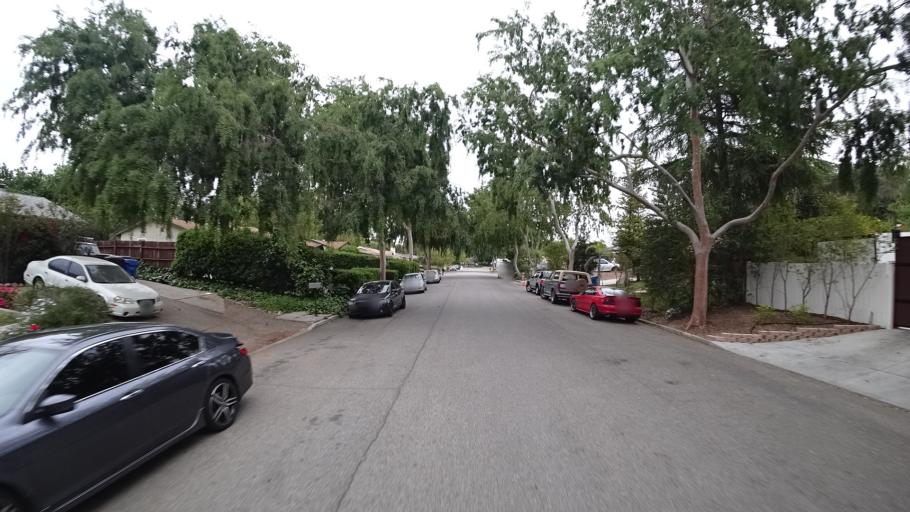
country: US
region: California
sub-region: Ventura County
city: Thousand Oaks
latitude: 34.2123
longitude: -118.8672
